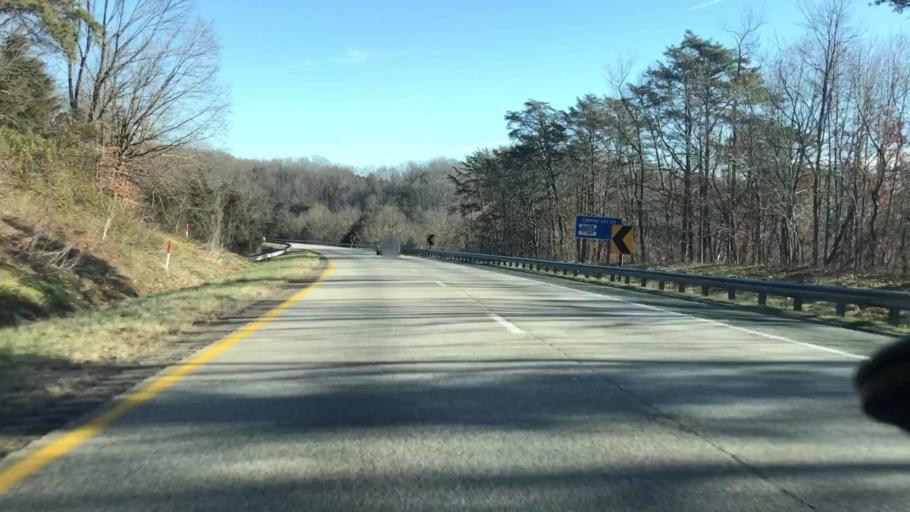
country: US
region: Virginia
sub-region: Botetourt County
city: Buchanan
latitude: 37.6112
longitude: -79.5961
